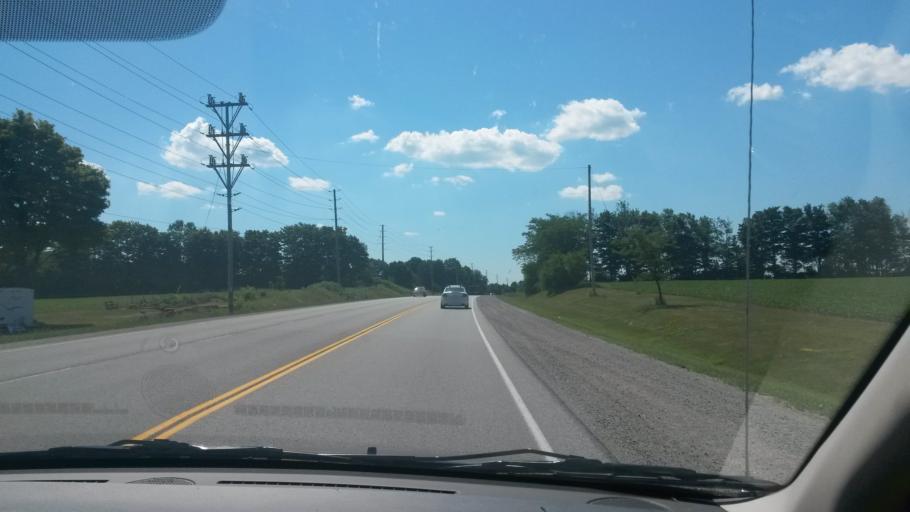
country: CA
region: Ontario
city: Barrie
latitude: 44.4971
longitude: -79.7868
